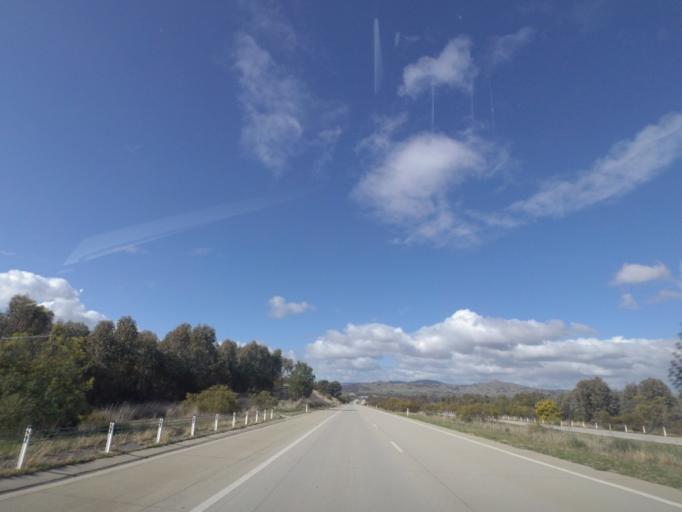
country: AU
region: New South Wales
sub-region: Albury Municipality
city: Lavington
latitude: -35.9153
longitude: 147.1135
